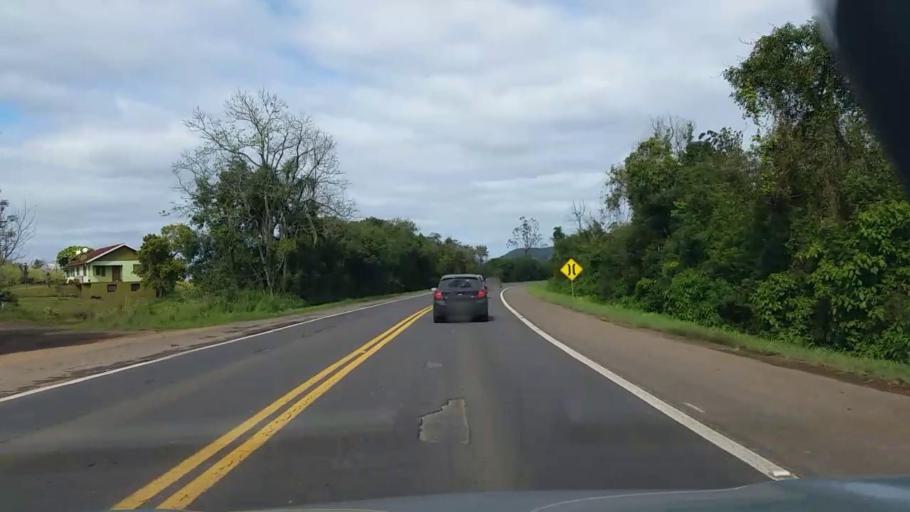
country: BR
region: Rio Grande do Sul
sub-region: Arroio Do Meio
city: Arroio do Meio
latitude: -29.3454
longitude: -52.0726
